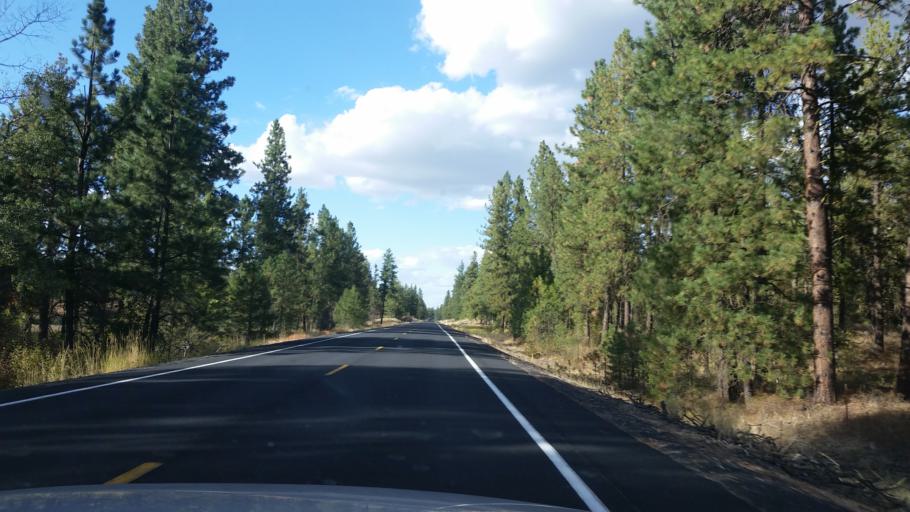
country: US
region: Washington
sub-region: Spokane County
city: Cheney
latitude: 47.4137
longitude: -117.5681
